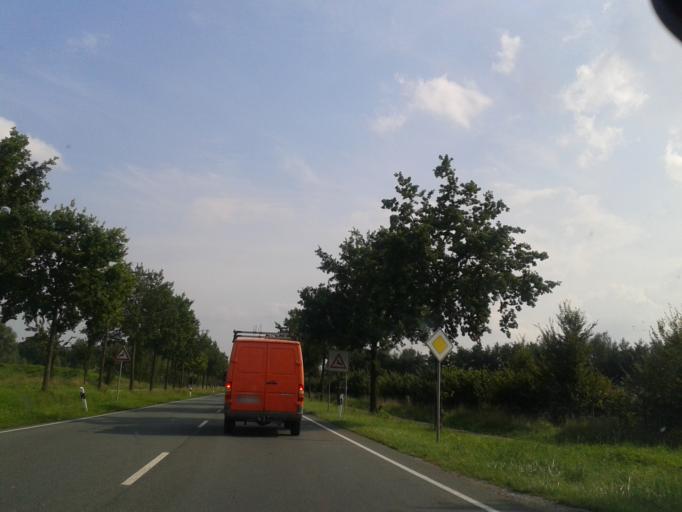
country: DE
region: North Rhine-Westphalia
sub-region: Regierungsbezirk Detmold
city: Paderborn
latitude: 51.7451
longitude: 8.7810
